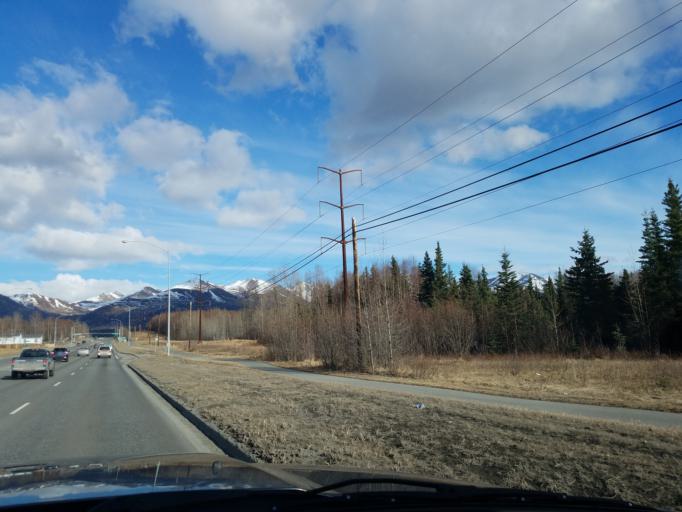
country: US
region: Alaska
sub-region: Anchorage Municipality
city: Anchorage
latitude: 61.1807
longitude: -149.7712
